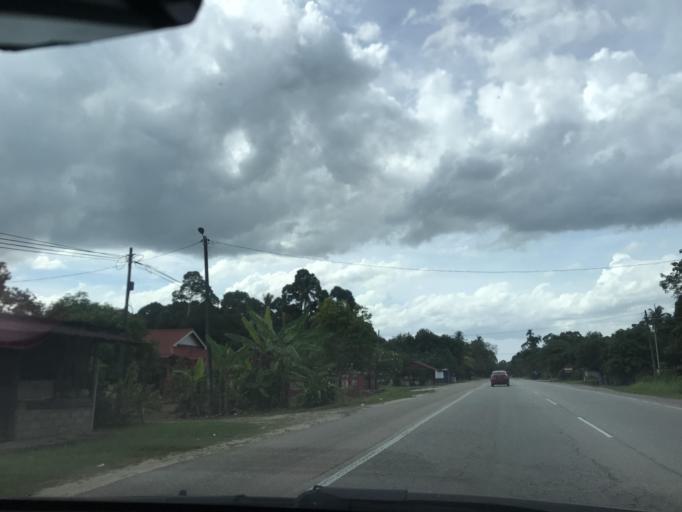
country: MY
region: Kelantan
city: Kampong Pangkal Kalong
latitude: 5.9311
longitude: 102.1909
